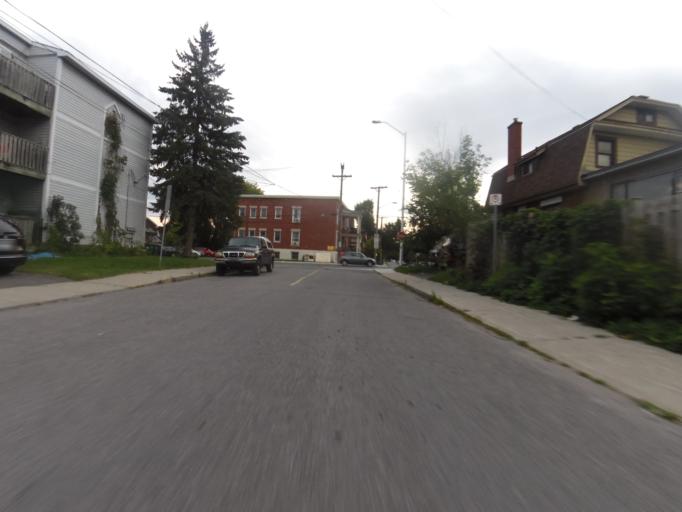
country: CA
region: Ontario
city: Ottawa
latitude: 45.4136
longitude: -75.6768
